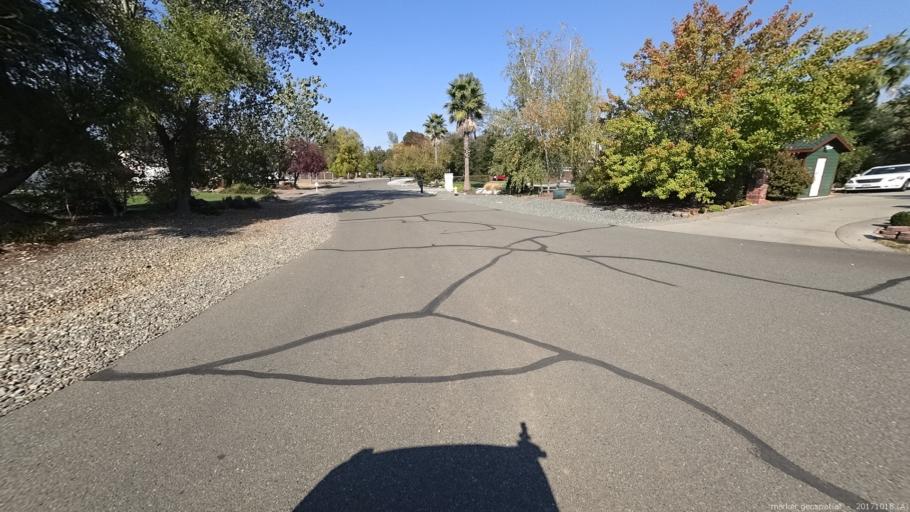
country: US
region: California
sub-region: Shasta County
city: Palo Cedro
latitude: 40.5572
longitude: -122.2331
